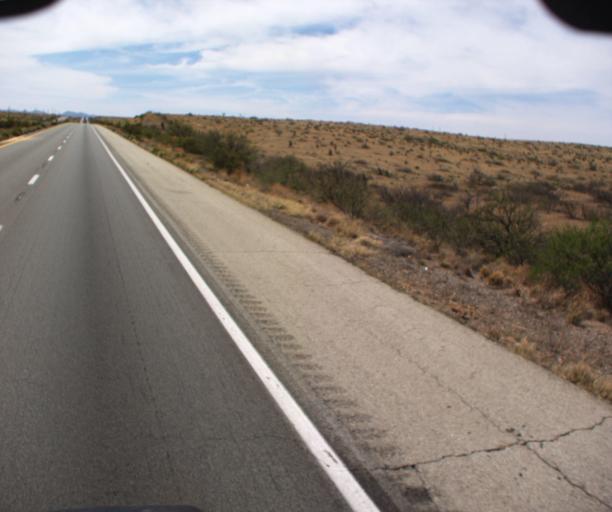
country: US
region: Arizona
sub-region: Cochise County
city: Willcox
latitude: 32.3551
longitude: -109.7069
